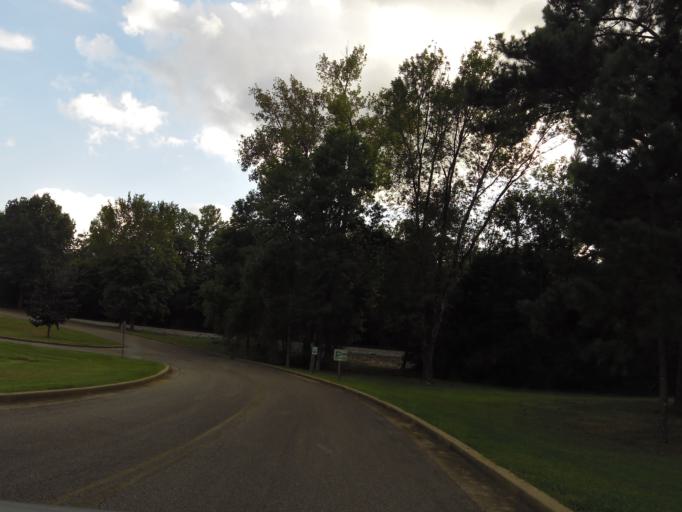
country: US
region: Mississippi
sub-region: Alcorn County
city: Corinth
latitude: 34.9379
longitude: -88.5316
